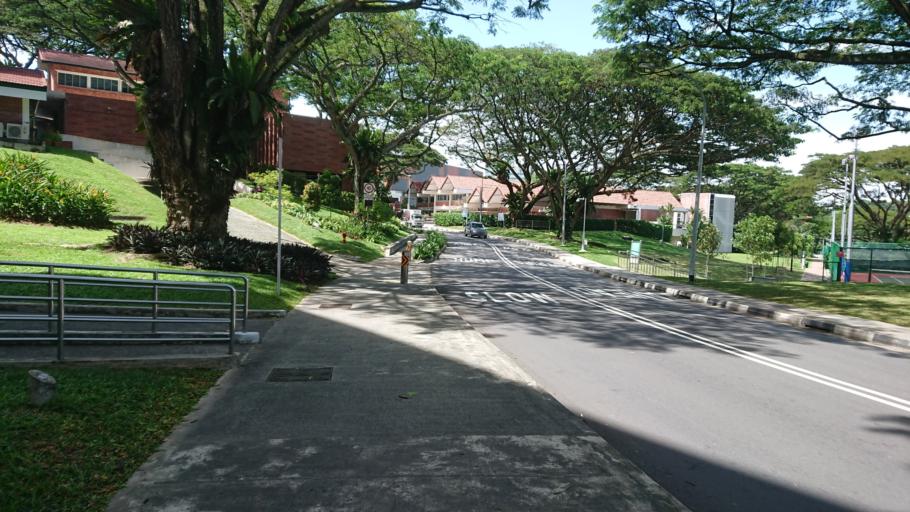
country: SG
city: Singapore
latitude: 1.2981
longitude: 103.7769
